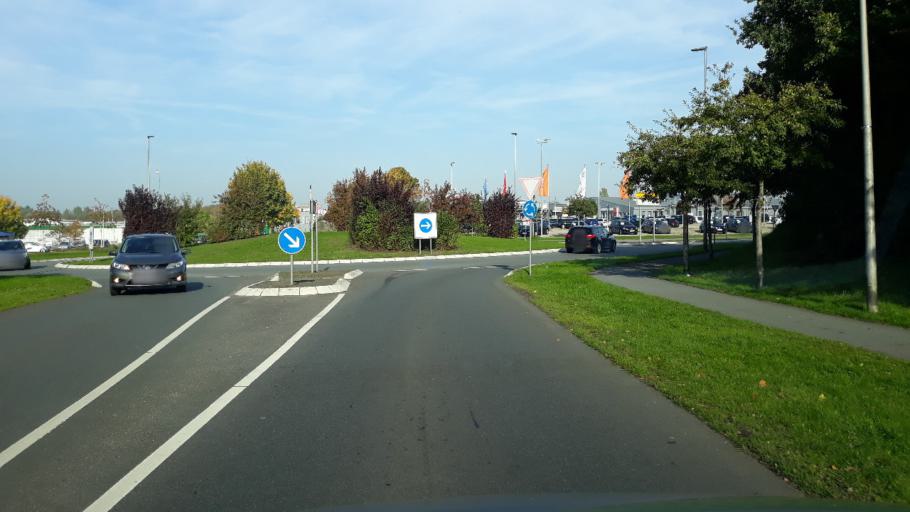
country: DE
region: Schleswig-Holstein
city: Schleswig
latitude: 54.5302
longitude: 9.5732
